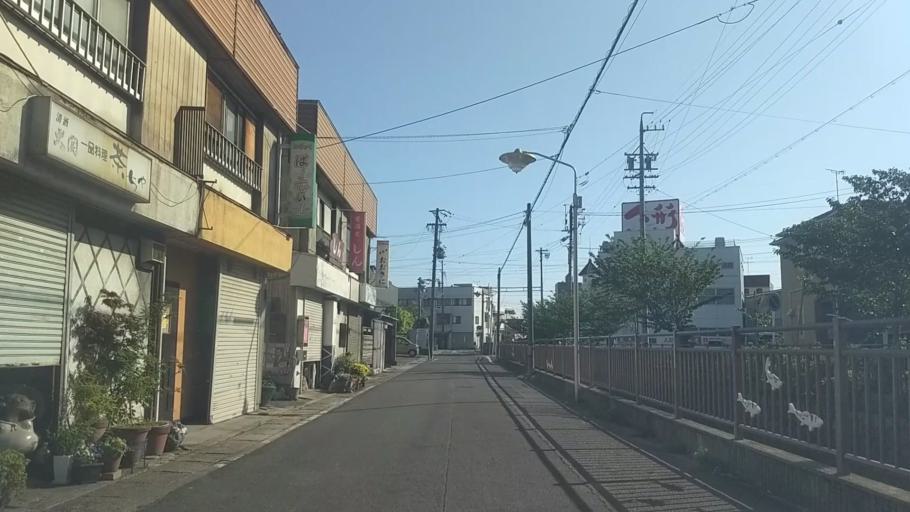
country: JP
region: Aichi
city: Anjo
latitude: 34.9580
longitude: 137.0888
